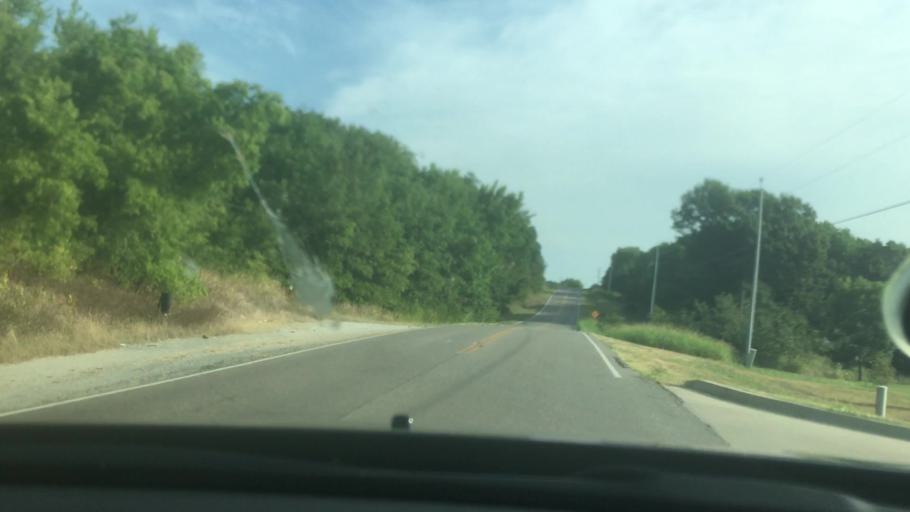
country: US
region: Oklahoma
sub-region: Pontotoc County
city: Ada
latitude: 34.7299
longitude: -96.6700
